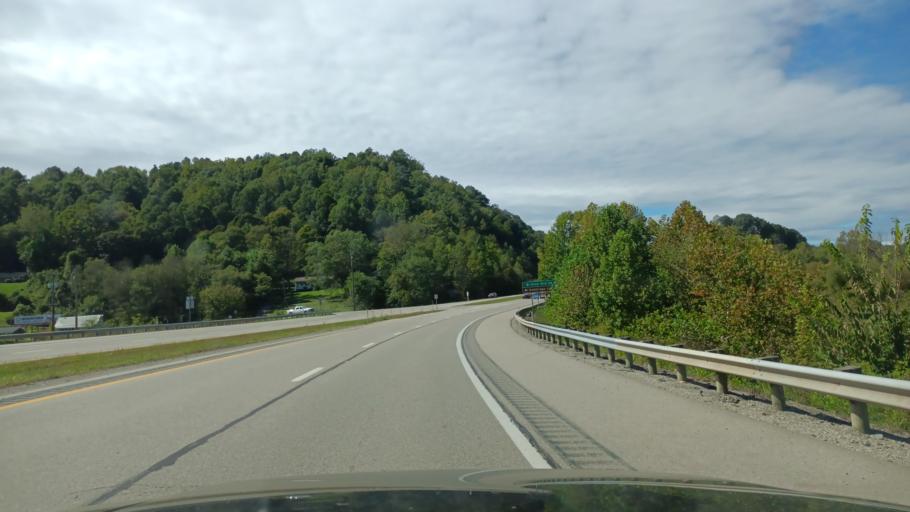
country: US
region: West Virginia
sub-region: Doddridge County
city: West Union
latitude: 39.2864
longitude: -80.7313
